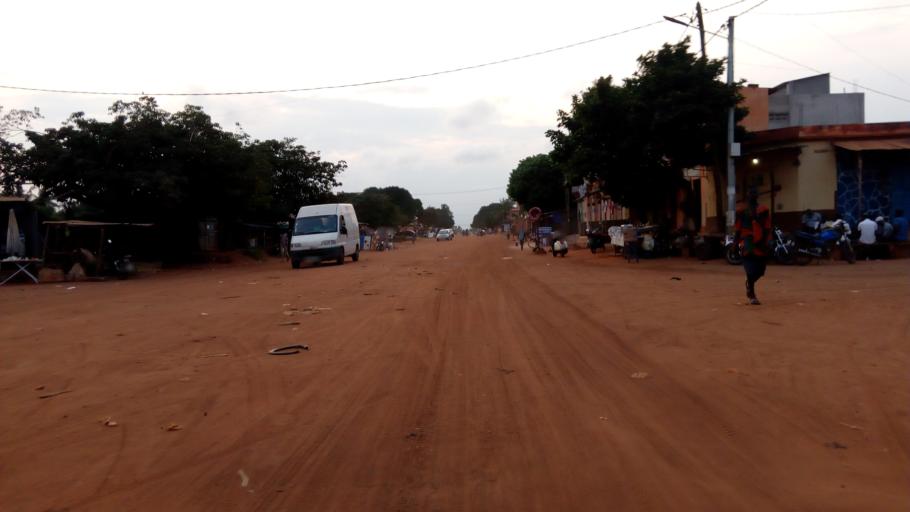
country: TG
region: Maritime
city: Lome
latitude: 6.2316
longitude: 1.1930
